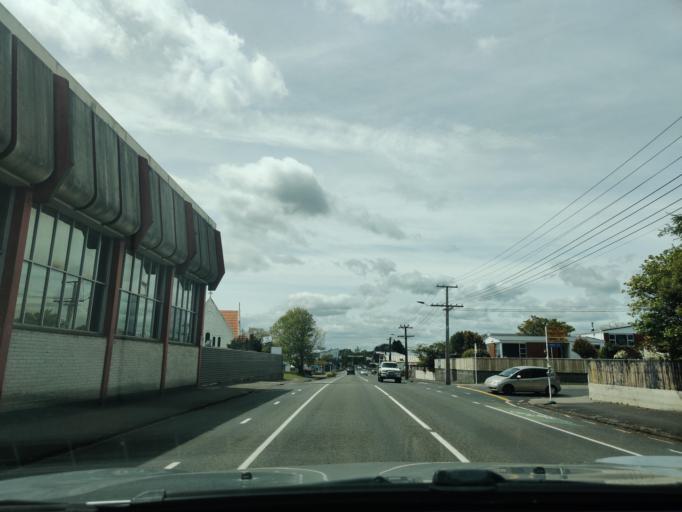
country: NZ
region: Taranaki
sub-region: New Plymouth District
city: New Plymouth
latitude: -39.1554
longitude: 174.2029
